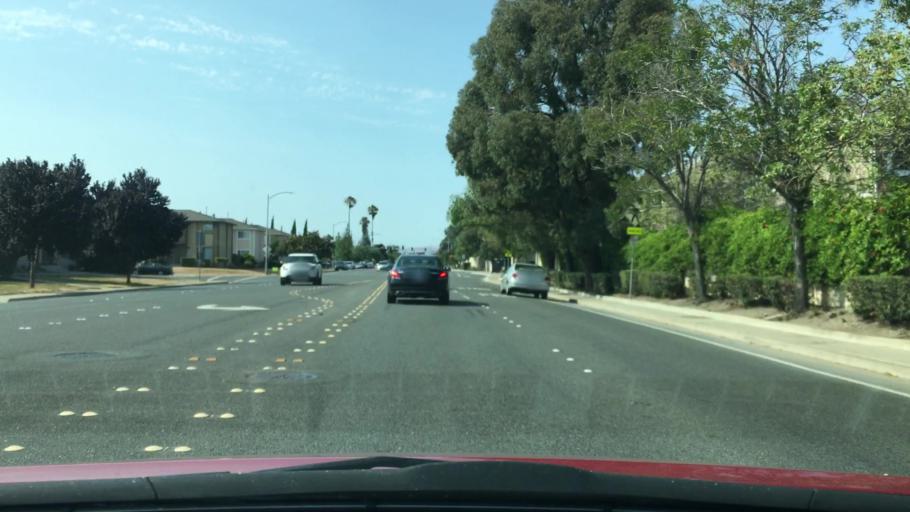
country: US
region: California
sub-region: Santa Clara County
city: Milpitas
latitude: 37.4338
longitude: -121.9098
